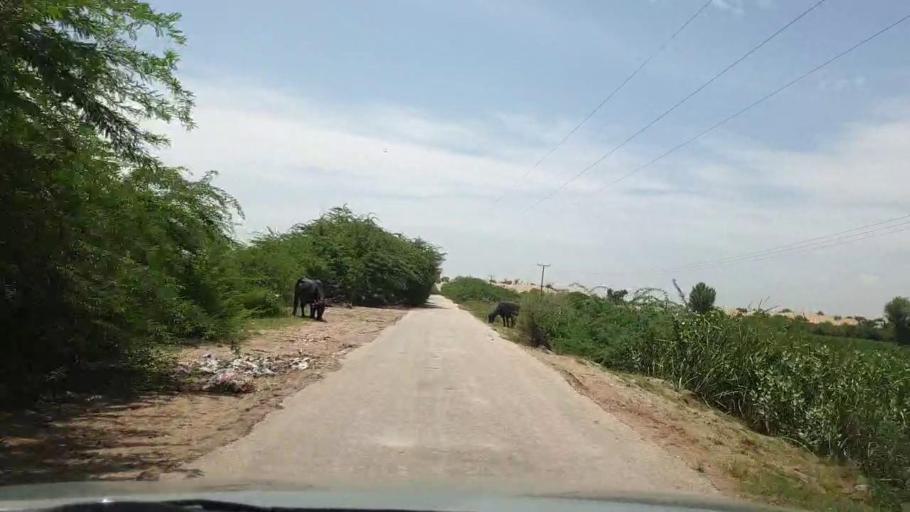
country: PK
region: Sindh
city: Bozdar
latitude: 27.0821
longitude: 68.9662
